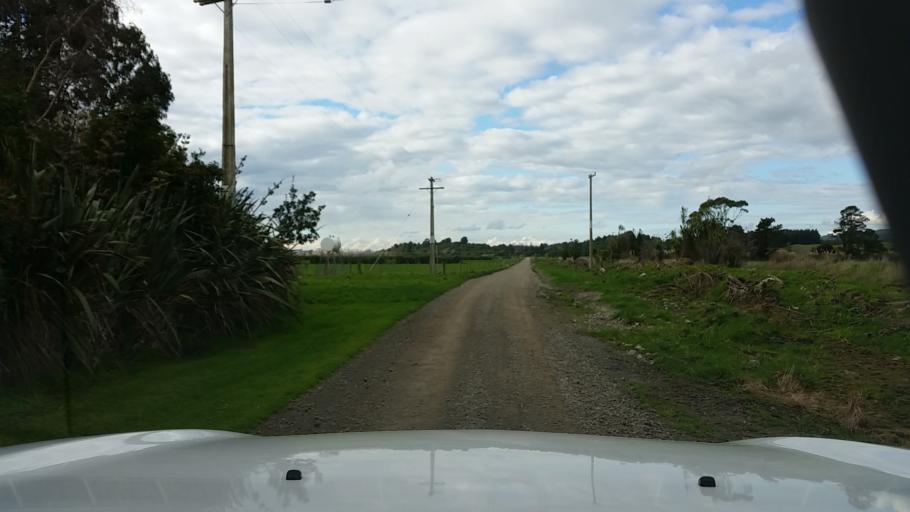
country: NZ
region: Wellington
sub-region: Upper Hutt City
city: Upper Hutt
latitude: -41.3011
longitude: 175.2608
